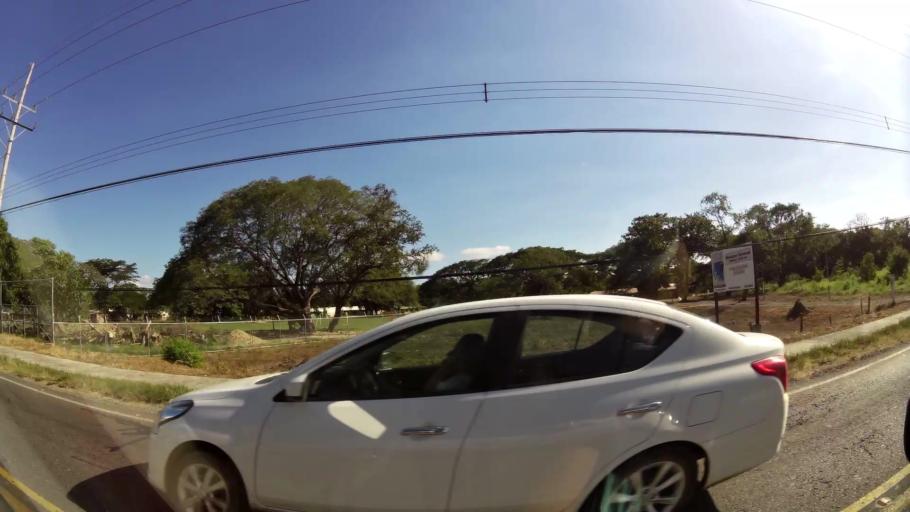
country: CR
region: Guanacaste
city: Liberia
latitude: 10.6212
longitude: -85.4550
